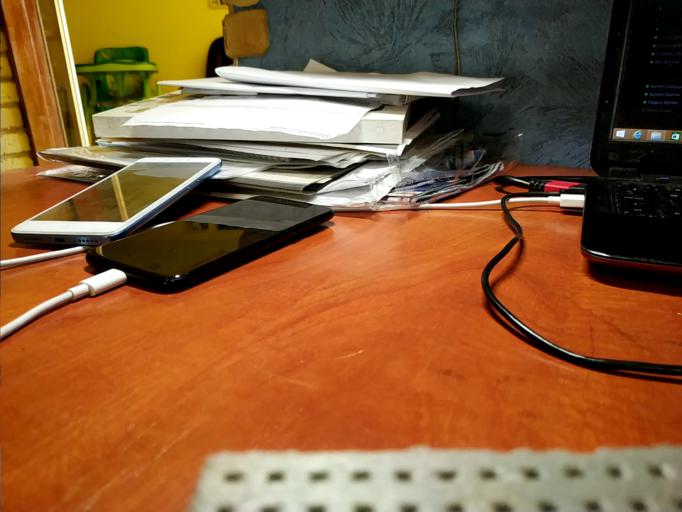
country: RU
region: Tverskaya
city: Spirovo
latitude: 57.4274
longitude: 35.0659
